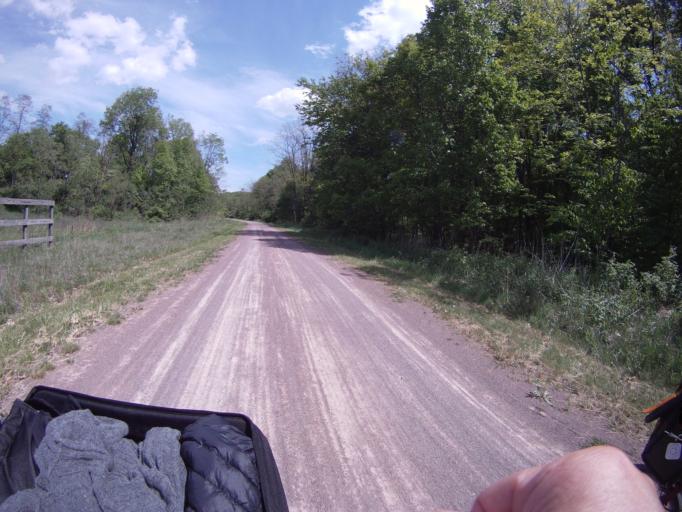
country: US
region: Pennsylvania
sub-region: Somerset County
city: Meyersdale
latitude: 39.7974
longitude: -78.9820
